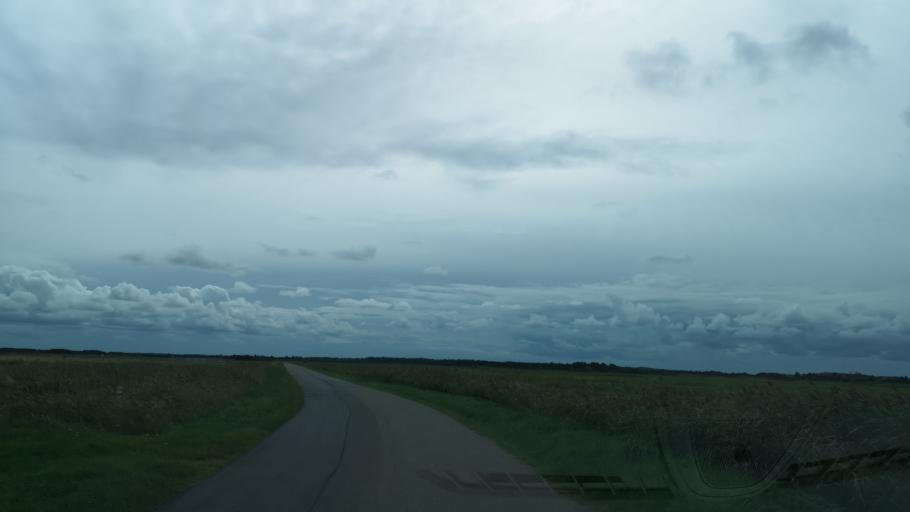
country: DK
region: Central Jutland
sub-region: Ringkobing-Skjern Kommune
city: Hvide Sande
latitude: 55.8493
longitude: 8.2176
